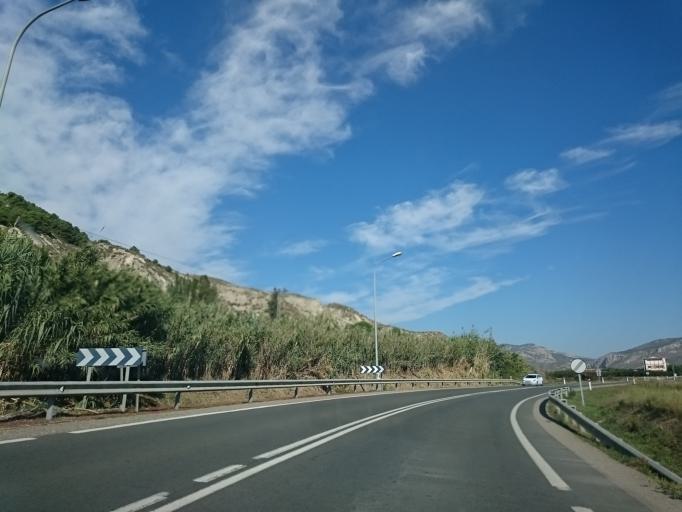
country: ES
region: Catalonia
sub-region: Provincia de Lleida
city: Alfarras
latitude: 41.8359
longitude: 0.5676
